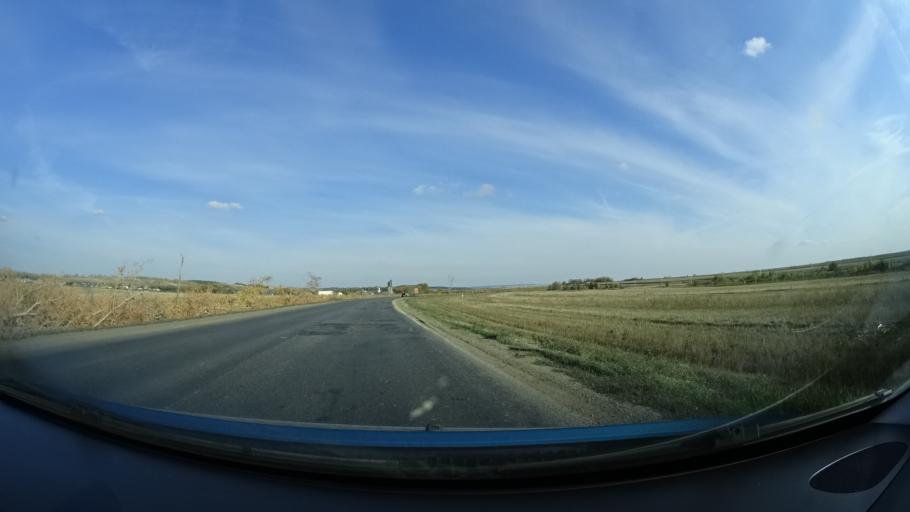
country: RU
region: Bashkortostan
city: Buzdyak
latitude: 54.6266
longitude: 54.4397
